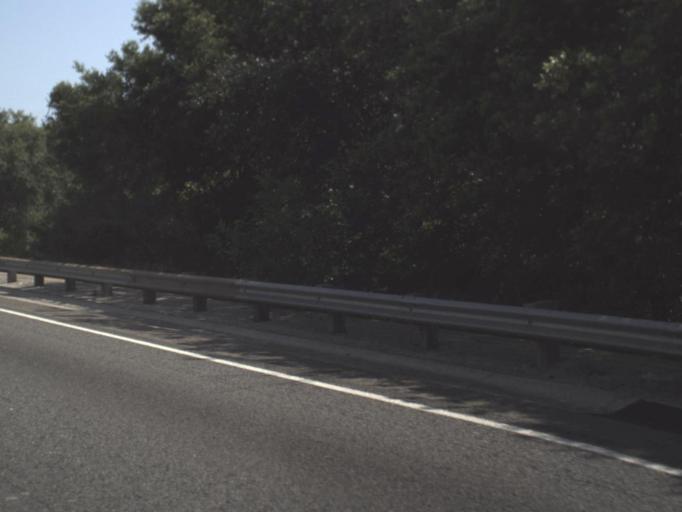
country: US
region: Florida
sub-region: Duval County
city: Jacksonville
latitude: 30.3525
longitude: -81.6684
